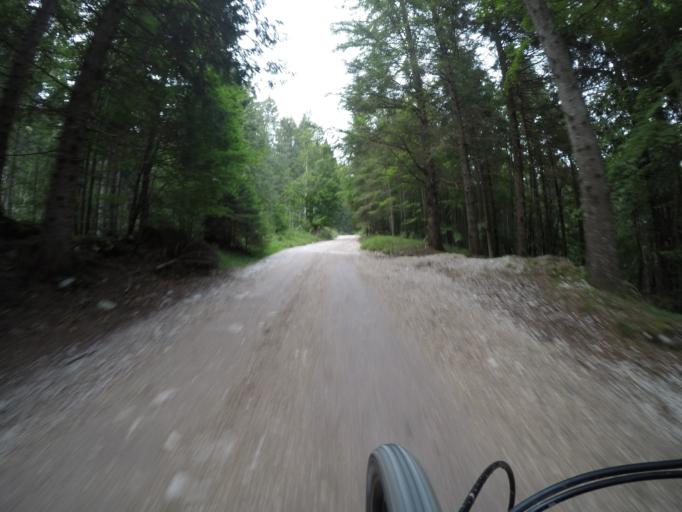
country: IT
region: Veneto
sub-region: Provincia di Vicenza
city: Gallio
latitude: 45.9113
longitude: 11.5243
